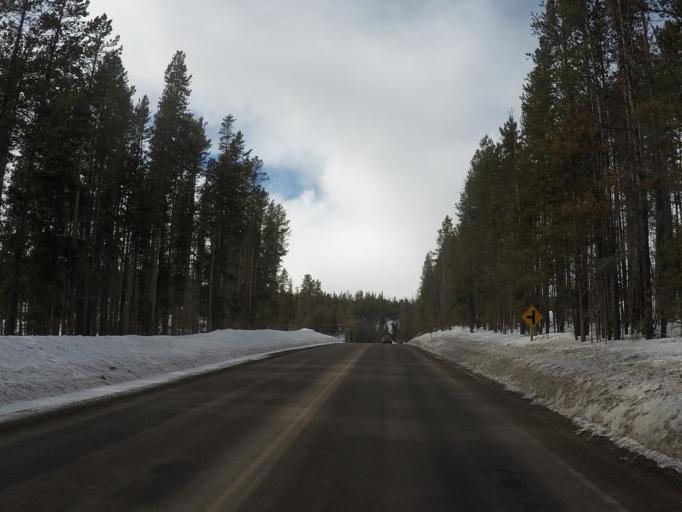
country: US
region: Montana
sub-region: Granite County
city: Philipsburg
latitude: 46.2141
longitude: -113.2781
